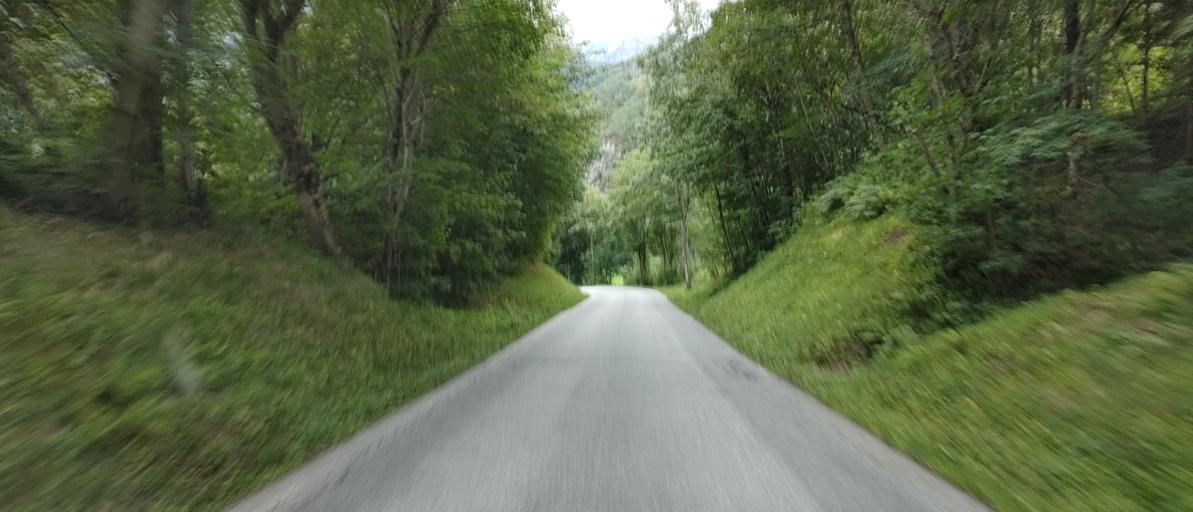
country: NO
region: More og Romsdal
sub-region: Rauma
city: Andalsnes
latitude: 62.5267
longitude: 7.7145
